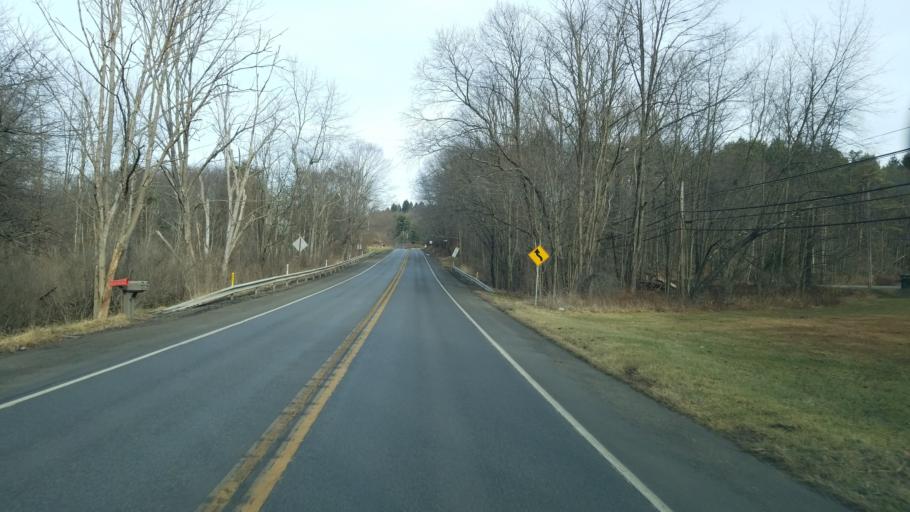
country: US
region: Pennsylvania
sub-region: Indiana County
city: Clymer
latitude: 40.6963
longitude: -78.9896
